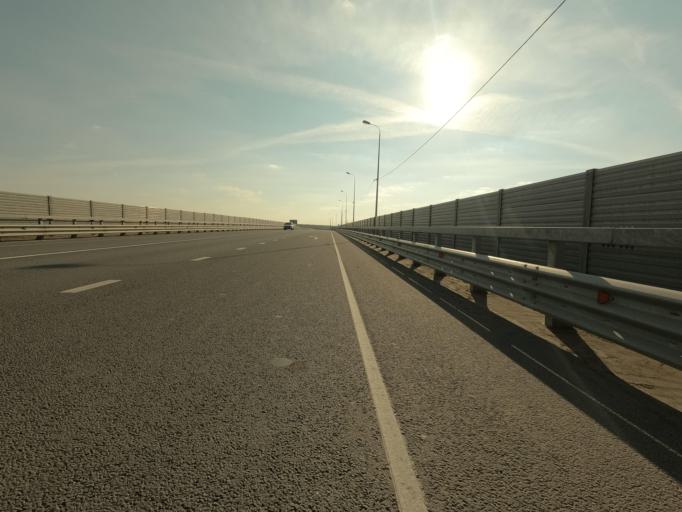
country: RU
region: Leningrad
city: Mga
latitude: 59.7555
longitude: 31.0922
